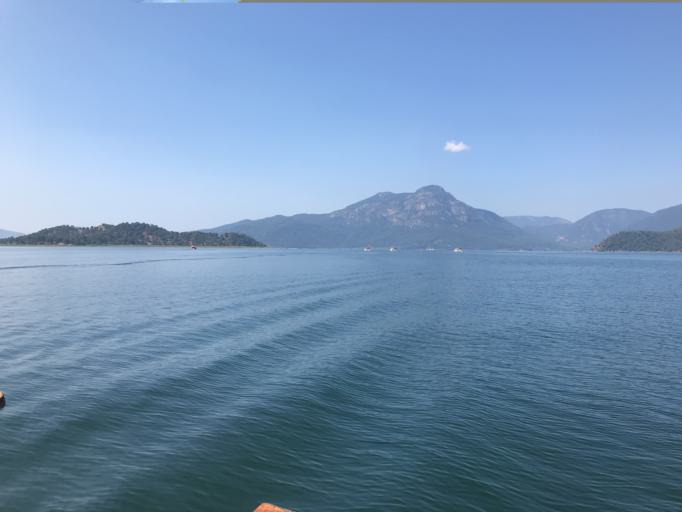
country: TR
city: Dalyan
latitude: 36.9124
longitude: 28.6545
